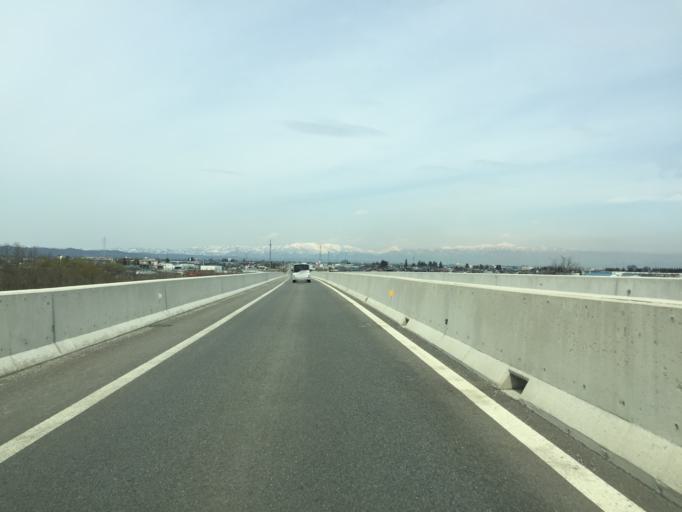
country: JP
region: Yamagata
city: Yonezawa
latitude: 37.9351
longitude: 140.1308
